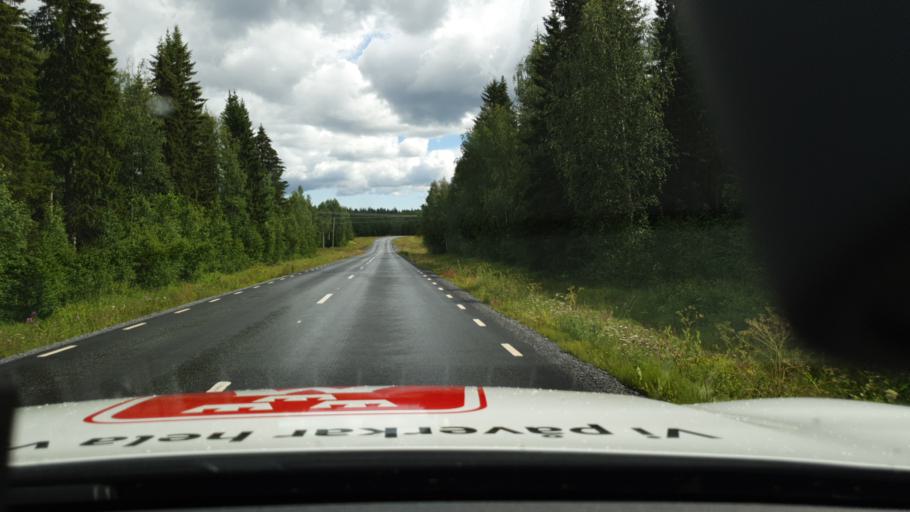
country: SE
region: Norrbotten
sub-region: Bodens Kommun
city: Saevast
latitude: 65.8444
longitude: 21.7837
